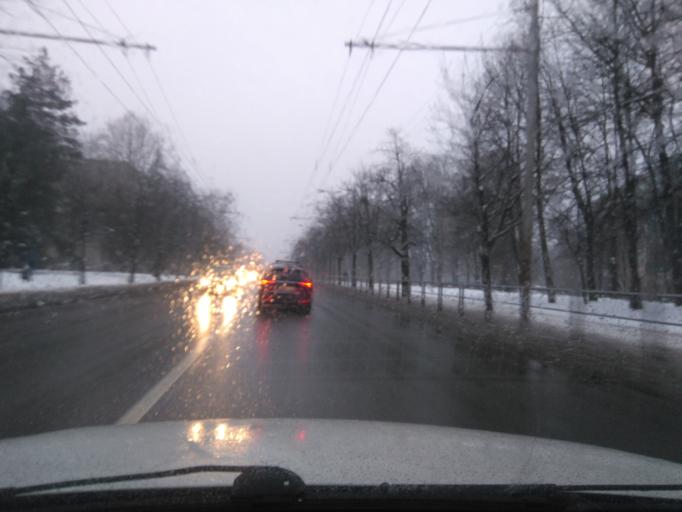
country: LT
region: Kauno apskritis
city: Dainava (Kaunas)
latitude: 54.9080
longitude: 23.9738
